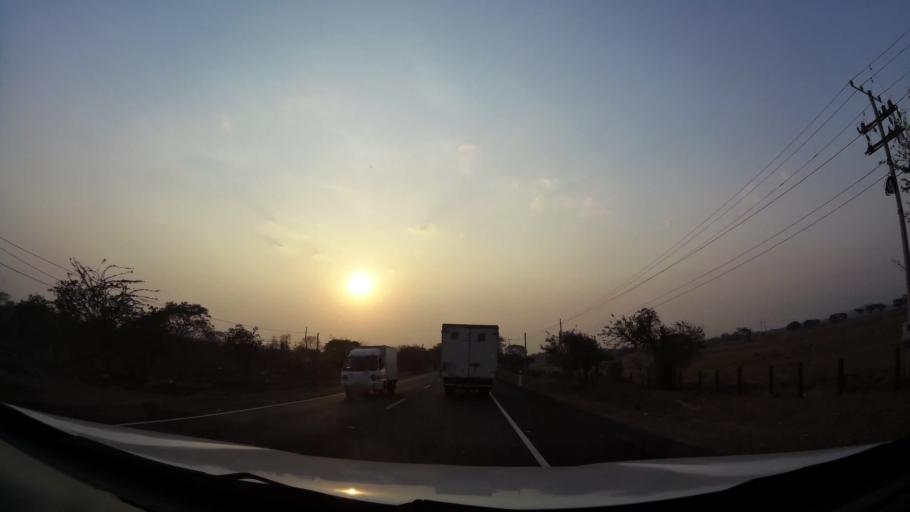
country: NI
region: Leon
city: La Paz Centro
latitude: 12.3325
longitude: -86.6492
